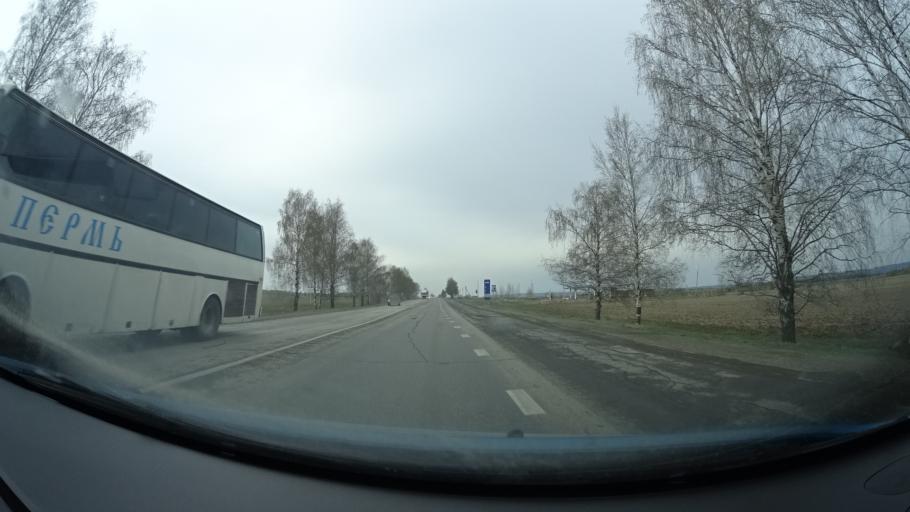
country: RU
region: Perm
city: Ust'-Kachka
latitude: 58.0715
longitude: 55.6338
